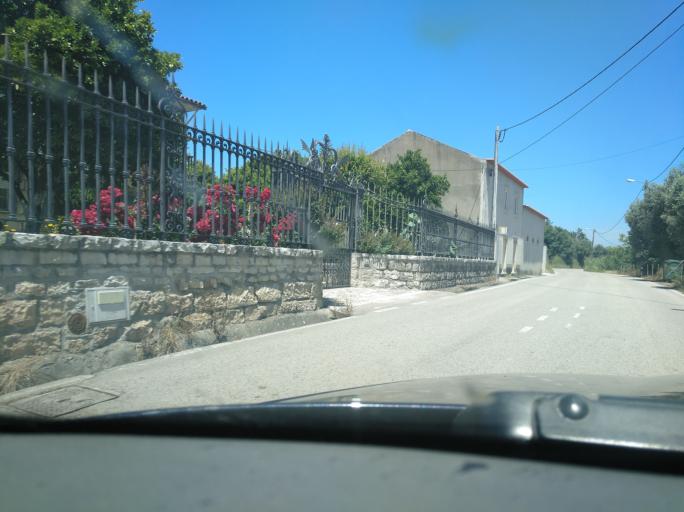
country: PT
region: Aveiro
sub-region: Mealhada
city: Pampilhosa do Botao
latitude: 40.2727
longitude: -8.4349
